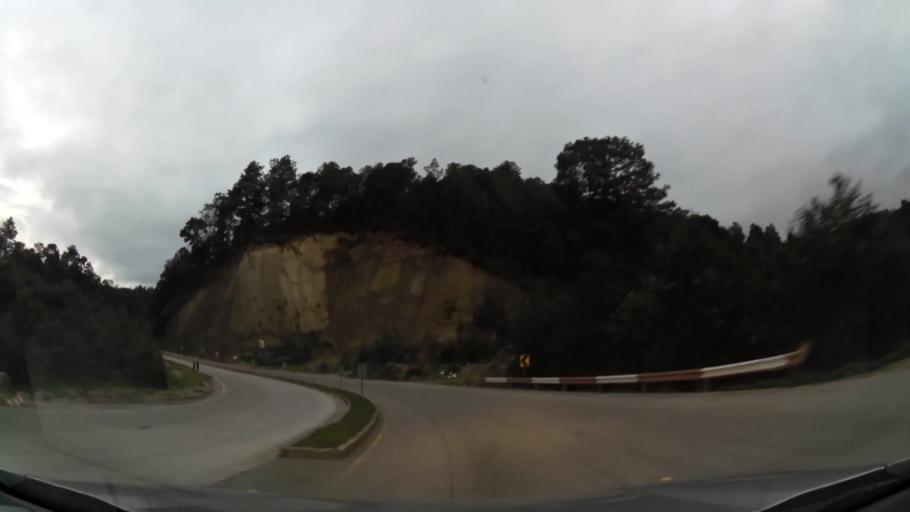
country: GT
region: Chimaltenango
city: Santa Apolonia
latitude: 14.8445
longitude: -91.0493
